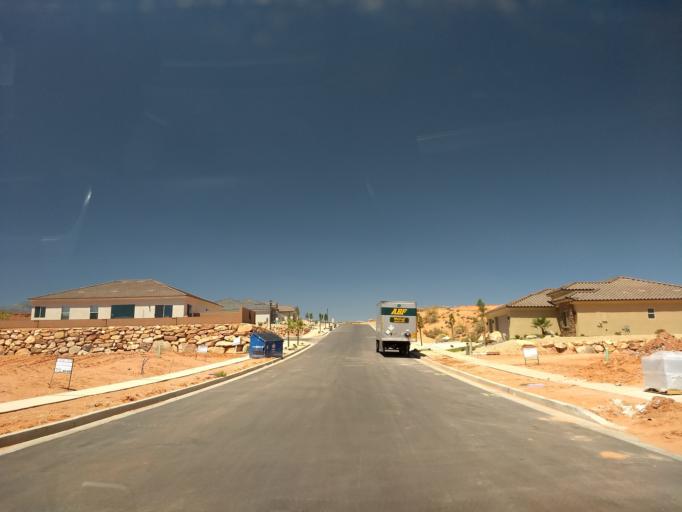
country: US
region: Utah
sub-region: Washington County
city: Washington
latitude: 37.1401
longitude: -113.4801
